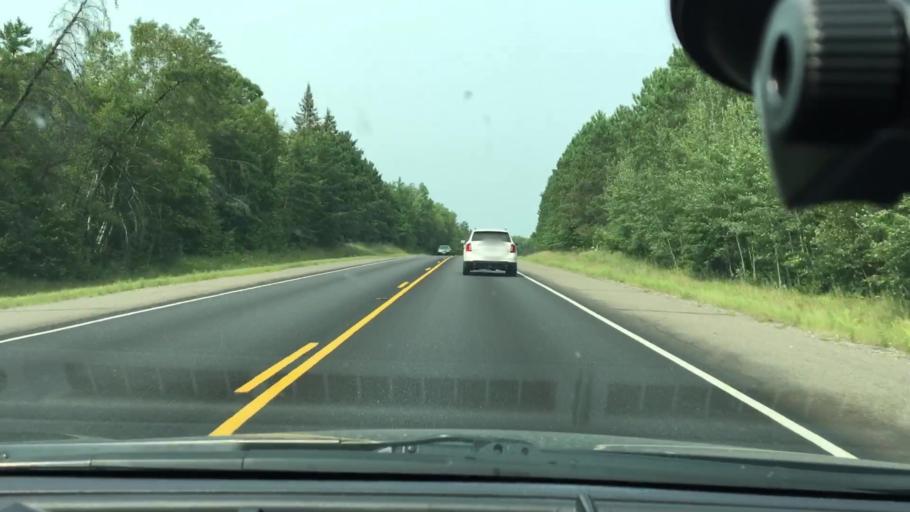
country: US
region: Minnesota
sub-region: Crow Wing County
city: Cross Lake
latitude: 46.6211
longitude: -94.1319
